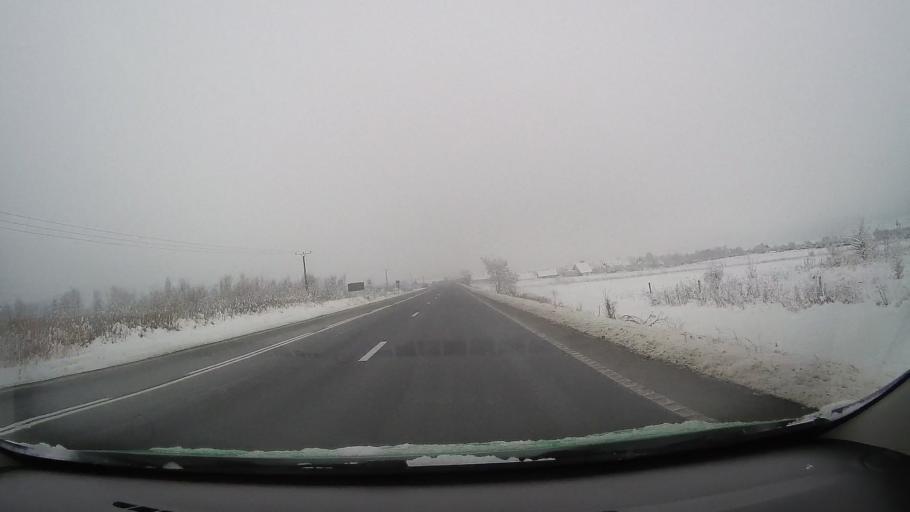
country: RO
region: Sibiu
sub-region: Oras Saliste
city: Saliste
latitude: 45.7880
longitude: 23.9293
